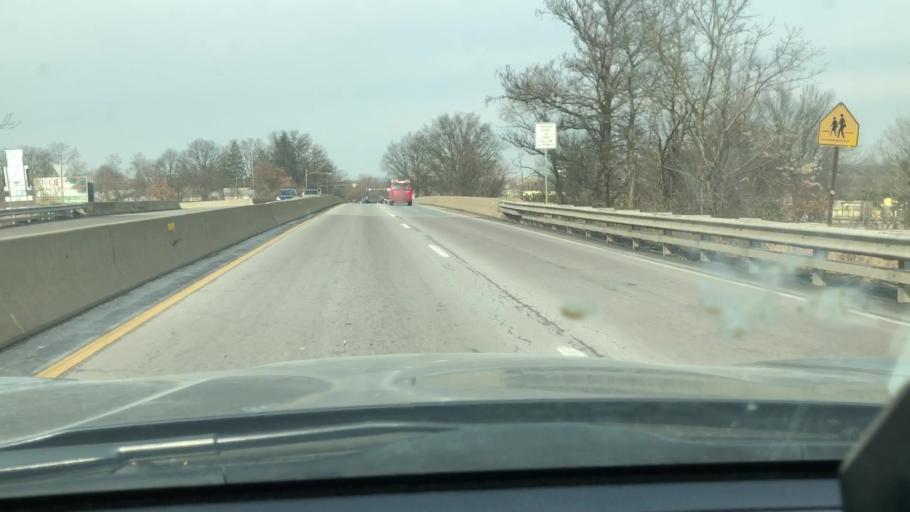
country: US
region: Pennsylvania
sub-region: Montgomery County
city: Pottstown
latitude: 40.2466
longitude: -75.6606
